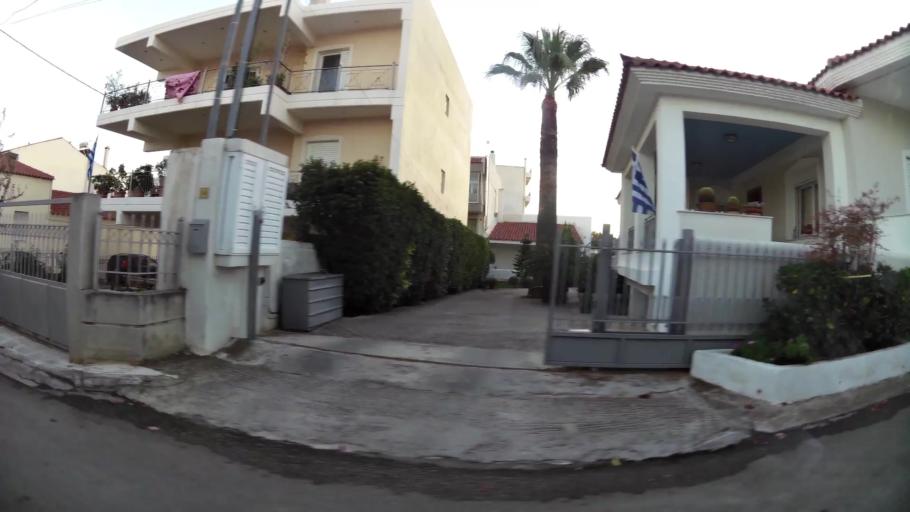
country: GR
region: Attica
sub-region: Nomarchia Anatolikis Attikis
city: Spata
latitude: 37.9635
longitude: 23.9176
